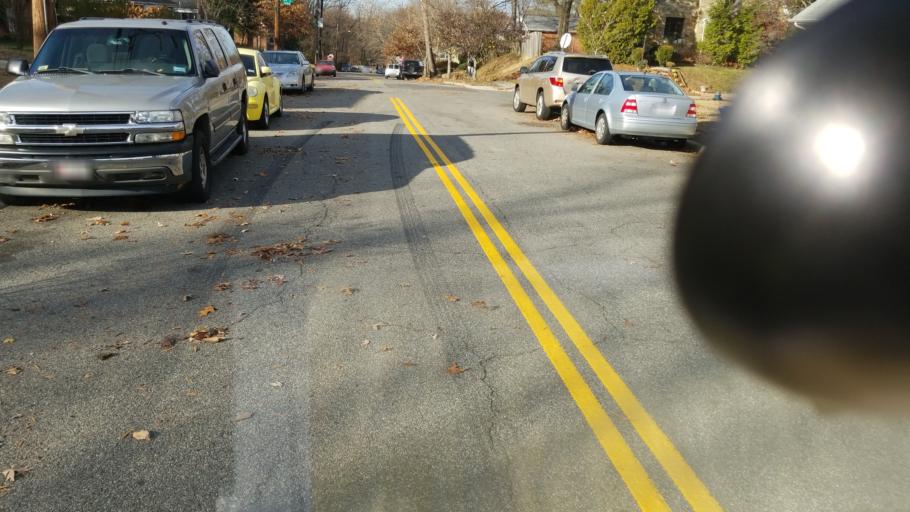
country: US
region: Maryland
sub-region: Prince George's County
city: Silver Hill
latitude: 38.8746
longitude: -76.9562
